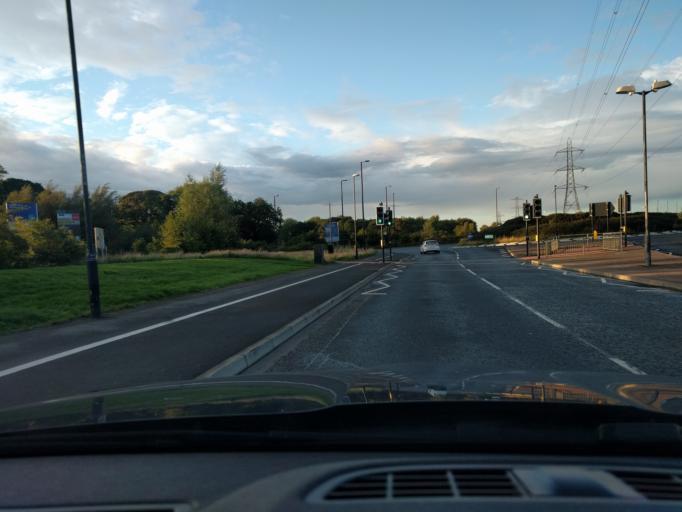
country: GB
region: England
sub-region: Northumberland
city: Backworth
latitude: 55.0364
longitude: -1.5244
